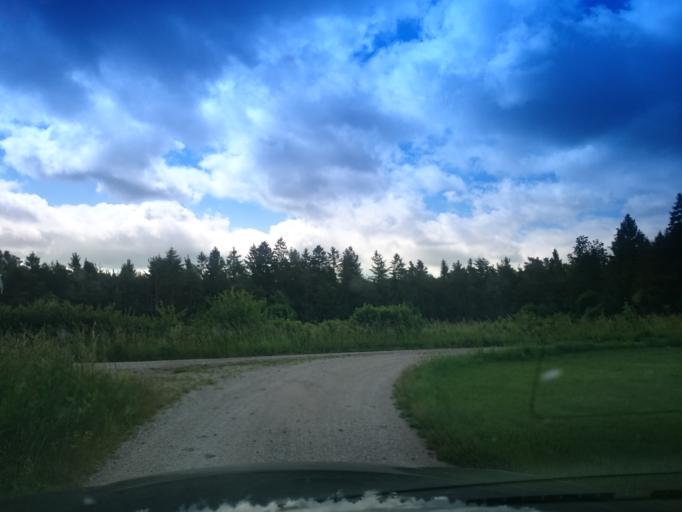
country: SE
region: Gotland
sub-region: Gotland
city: Slite
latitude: 57.4227
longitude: 18.6475
